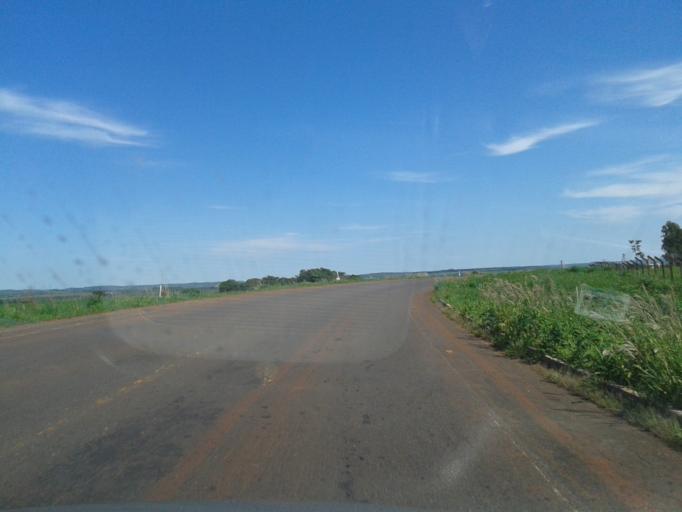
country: BR
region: Goias
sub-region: Piracanjuba
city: Piracanjuba
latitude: -17.1939
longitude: -48.7162
